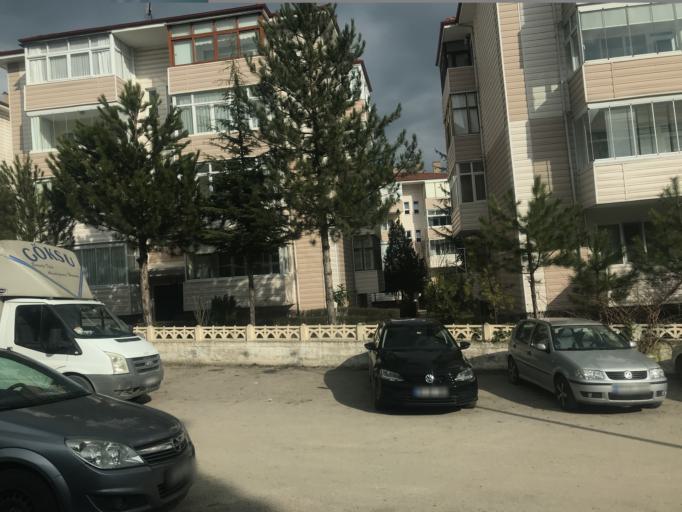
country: TR
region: Karabuk
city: Safranbolu
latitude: 41.2542
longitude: 32.6825
